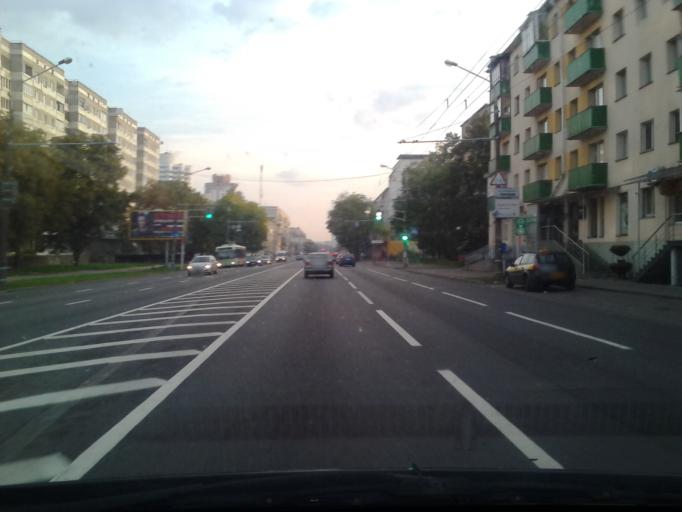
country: BY
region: Minsk
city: Minsk
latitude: 53.9184
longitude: 27.5653
